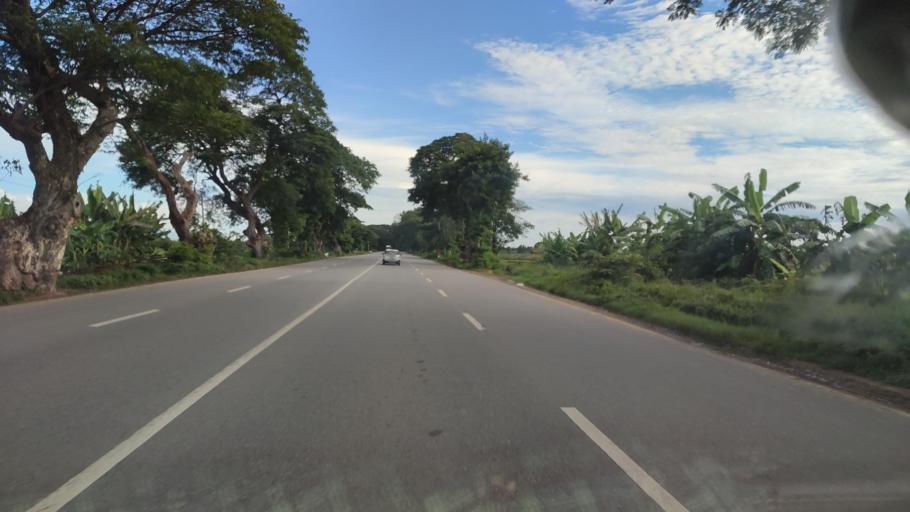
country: MM
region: Mandalay
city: Yamethin
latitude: 20.2329
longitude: 96.1792
